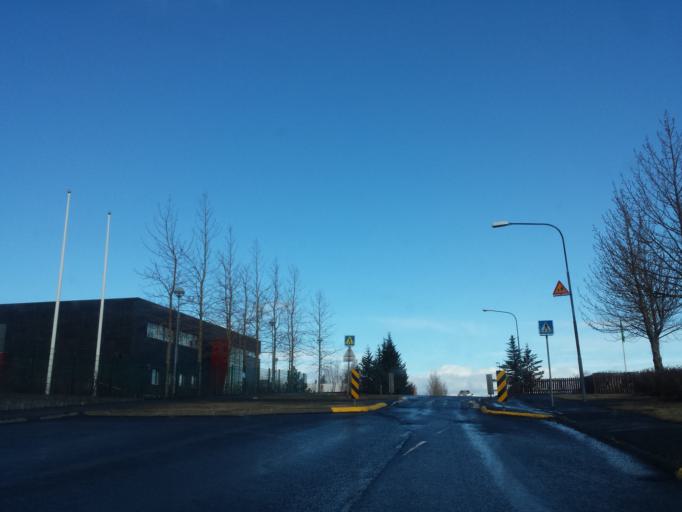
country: IS
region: Capital Region
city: Reykjavik
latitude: 64.1102
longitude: -21.8626
